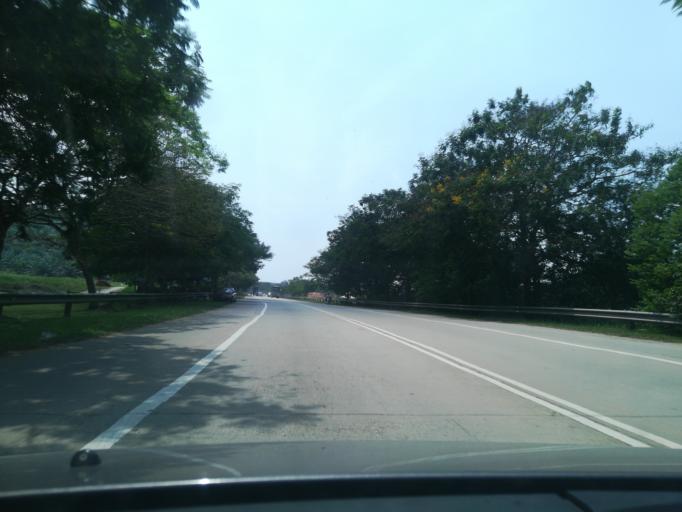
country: MY
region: Kedah
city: Kulim
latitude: 5.4282
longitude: 100.5583
